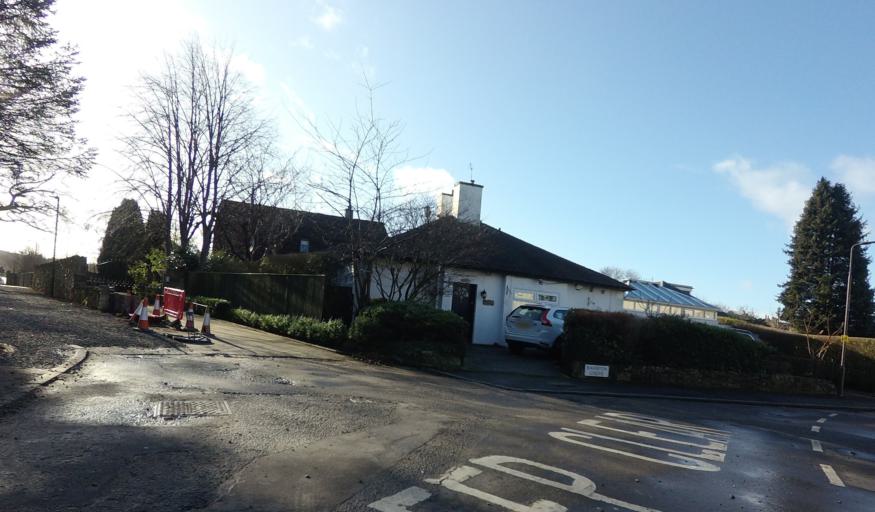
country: GB
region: Scotland
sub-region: Edinburgh
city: Currie
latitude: 55.9613
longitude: -3.3015
